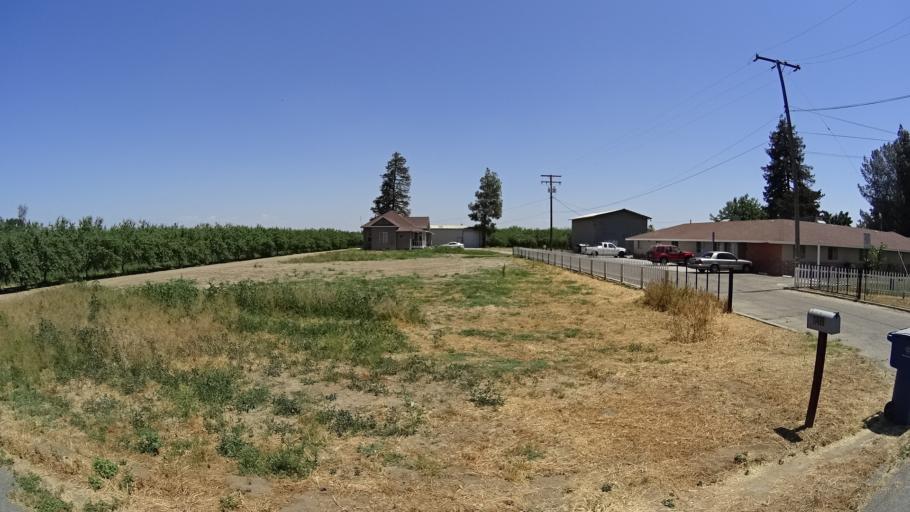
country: US
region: California
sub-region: Kings County
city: Armona
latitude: 36.3065
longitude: -119.7271
